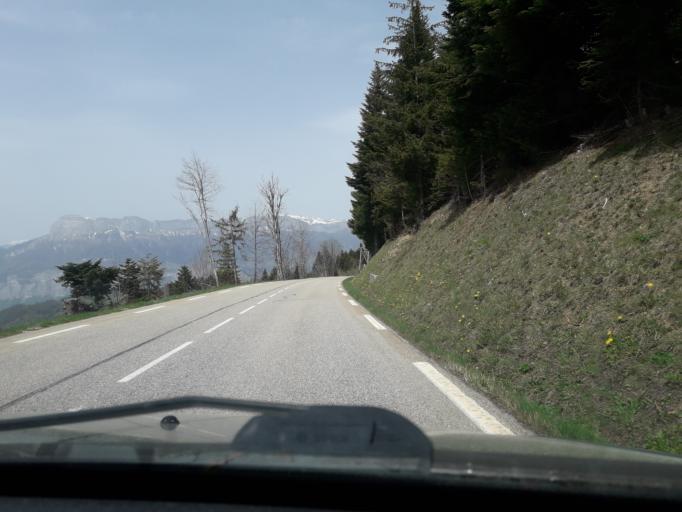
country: FR
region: Rhone-Alpes
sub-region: Departement de l'Isere
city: Theys
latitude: 45.2630
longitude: 5.9991
